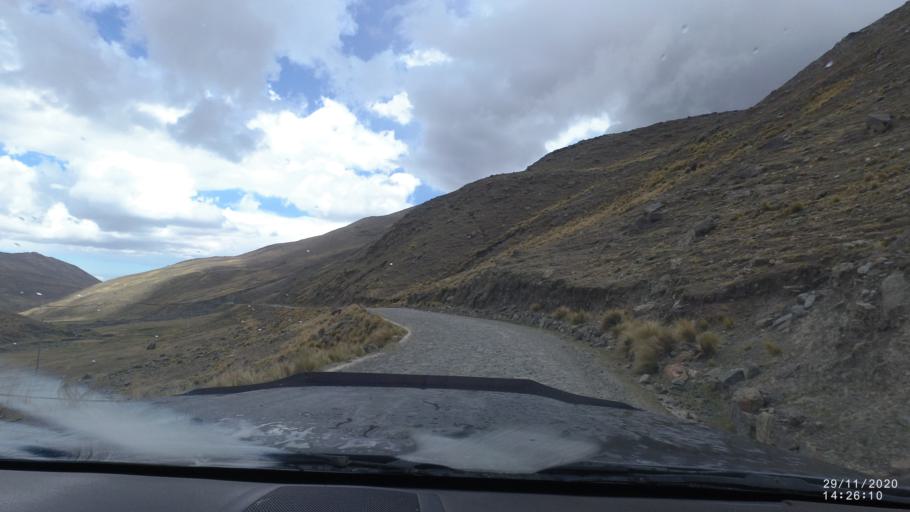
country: BO
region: Cochabamba
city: Sipe Sipe
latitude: -17.2563
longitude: -66.3723
